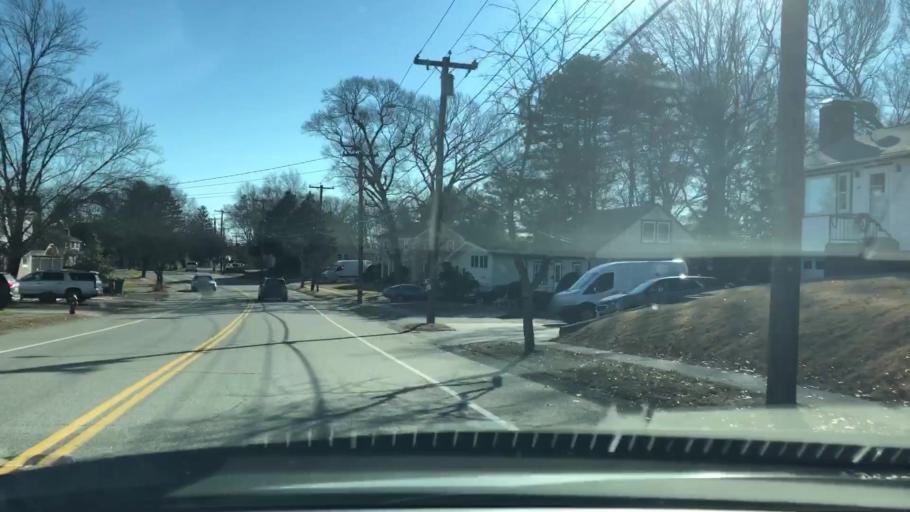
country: US
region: Massachusetts
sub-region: Norfolk County
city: Norwood
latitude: 42.1676
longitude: -71.2026
